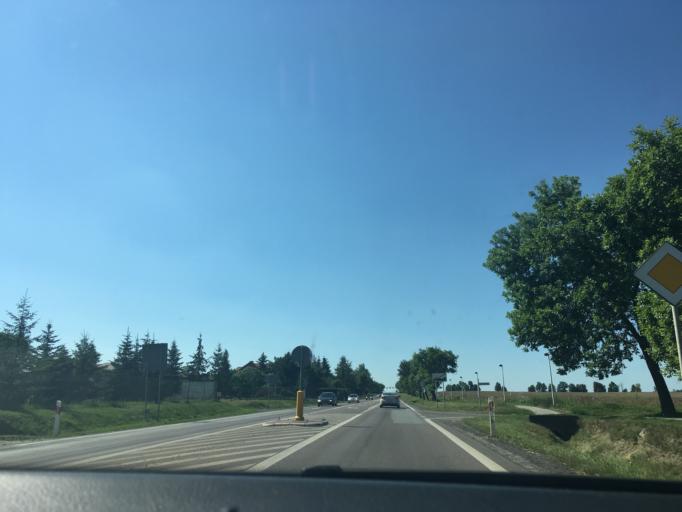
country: PL
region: Lublin Voivodeship
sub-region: Powiat lubelski
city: Niemce
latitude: 51.3551
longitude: 22.6208
